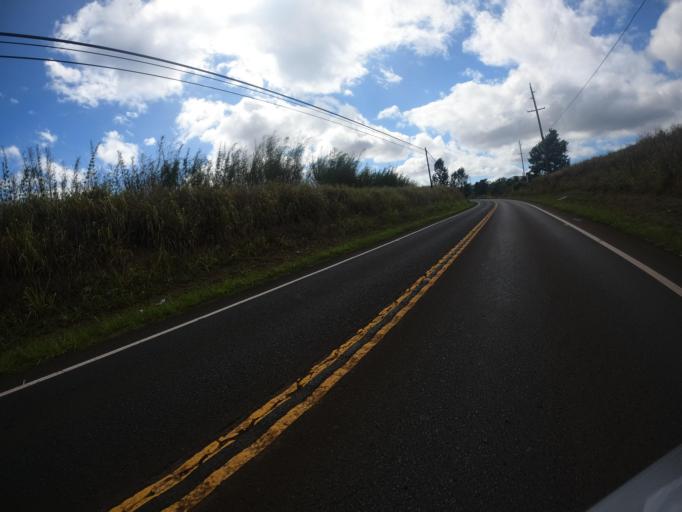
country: US
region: Hawaii
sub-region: Honolulu County
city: Schofield Barracks
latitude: 21.4546
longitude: -158.0604
